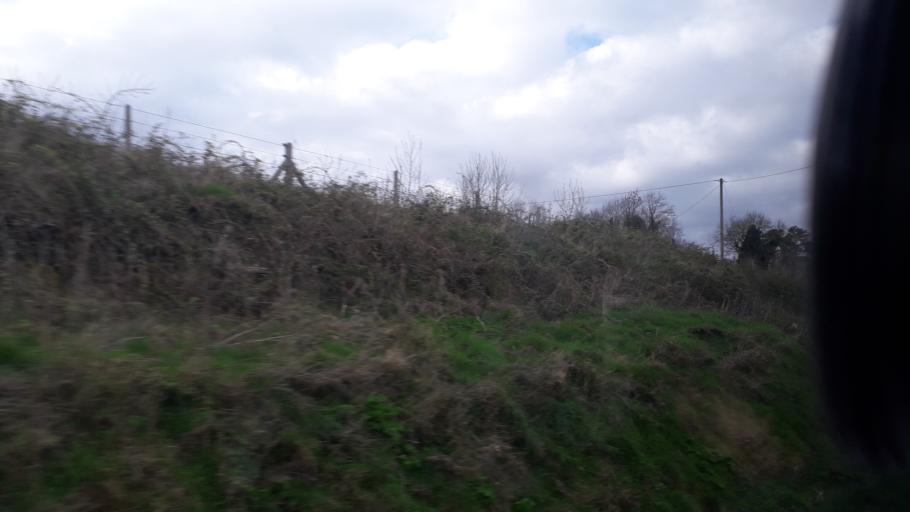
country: IE
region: Leinster
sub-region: An Iarmhi
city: An Muileann gCearr
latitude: 53.6283
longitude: -7.4172
